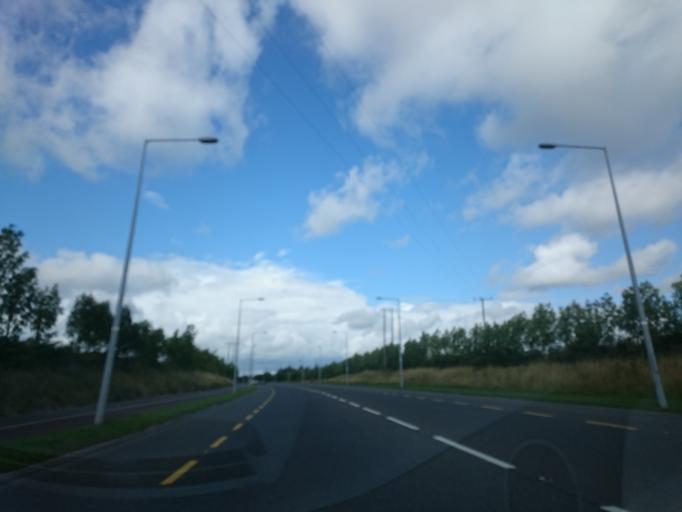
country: IE
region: Leinster
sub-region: Kilkenny
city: Kilkenny
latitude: 52.6744
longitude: -7.2358
